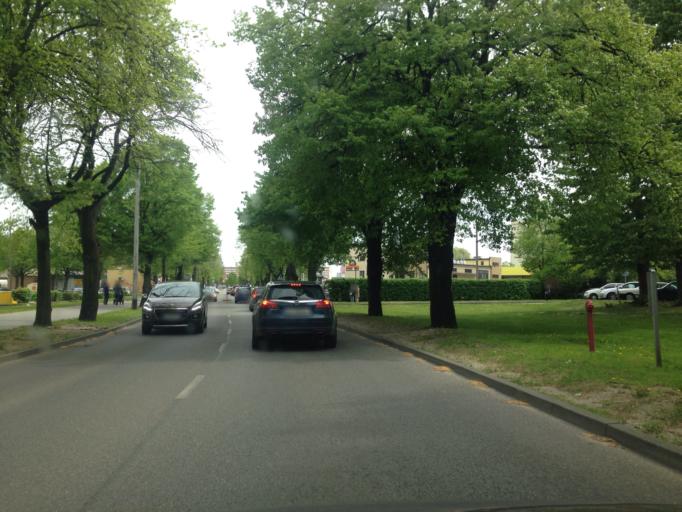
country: PL
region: Pomeranian Voivodeship
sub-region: Sopot
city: Sopot
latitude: 54.4219
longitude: 18.5807
